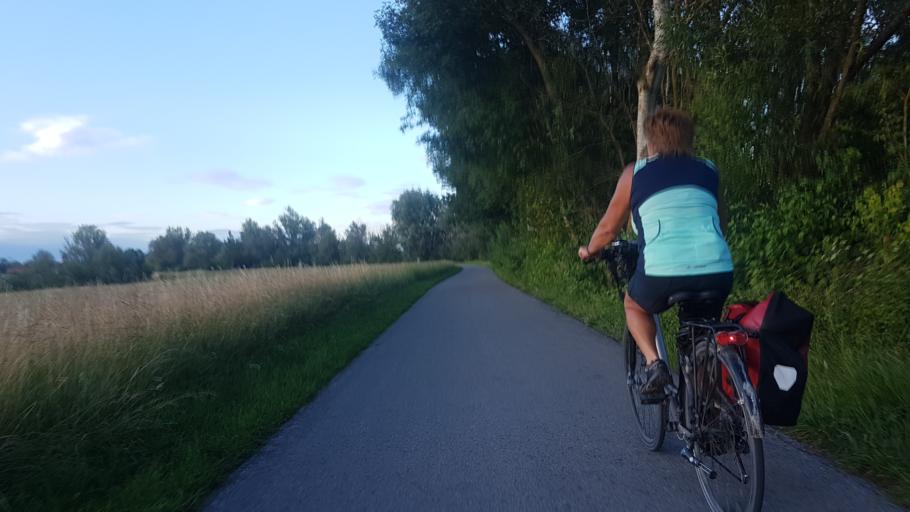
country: DE
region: Bavaria
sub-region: Regierungsbezirk Mittelfranken
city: Muhr am See
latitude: 49.1463
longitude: 10.7026
